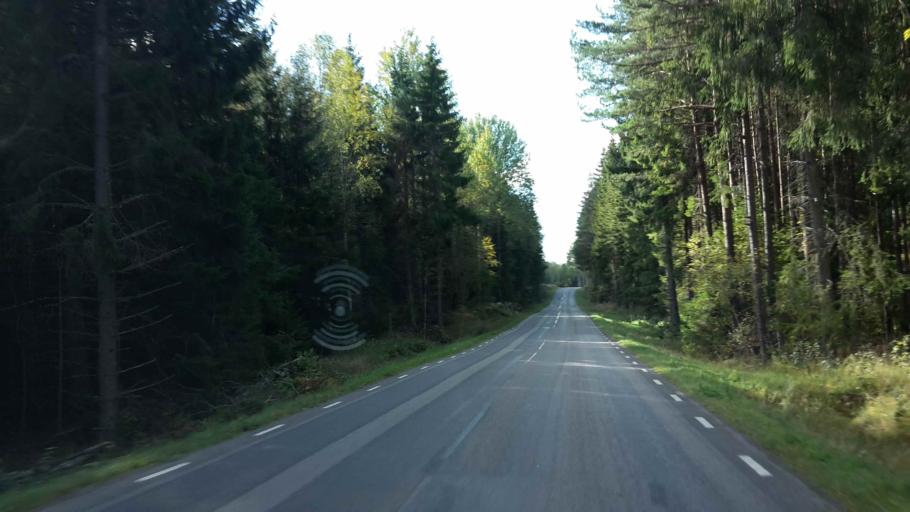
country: SE
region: OEstergoetland
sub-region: Atvidabergs Kommun
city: Atvidaberg
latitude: 58.1813
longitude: 16.0809
